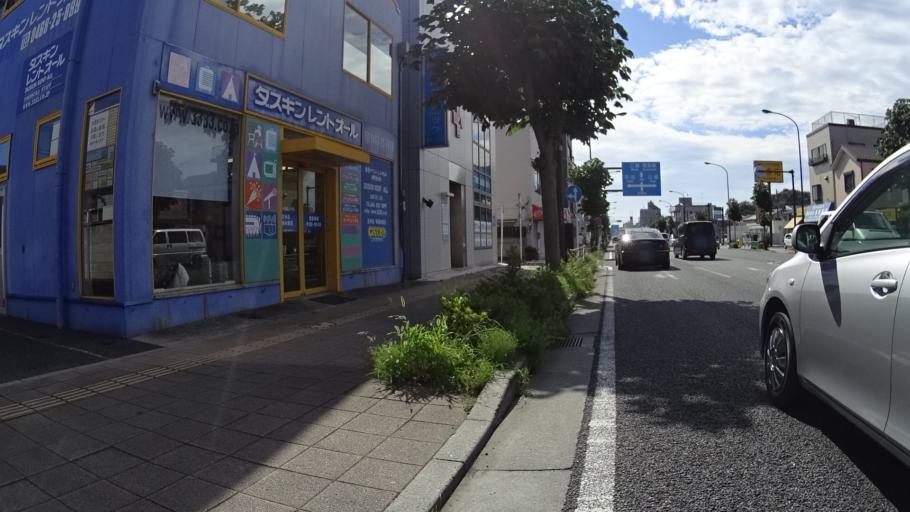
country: JP
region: Kanagawa
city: Yokosuka
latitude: 35.2692
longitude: 139.6817
